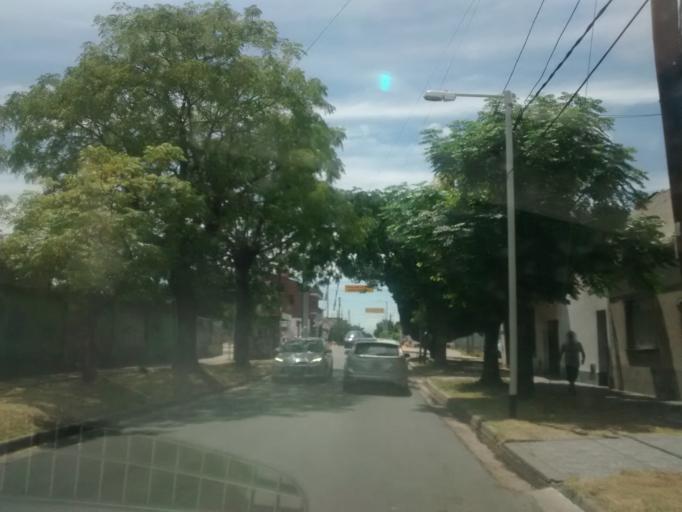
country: AR
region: Buenos Aires
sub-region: Partido de Avellaneda
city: Avellaneda
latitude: -34.6933
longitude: -58.3241
